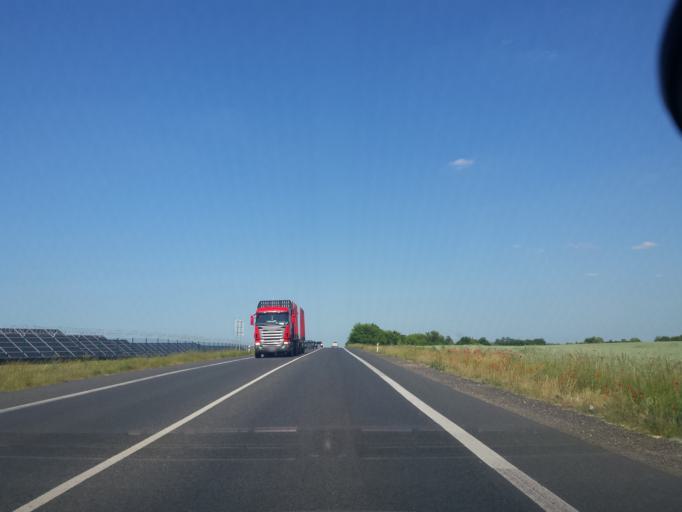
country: CZ
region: Central Bohemia
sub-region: Okres Melnik
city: Veltrusy
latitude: 50.3128
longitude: 14.3213
